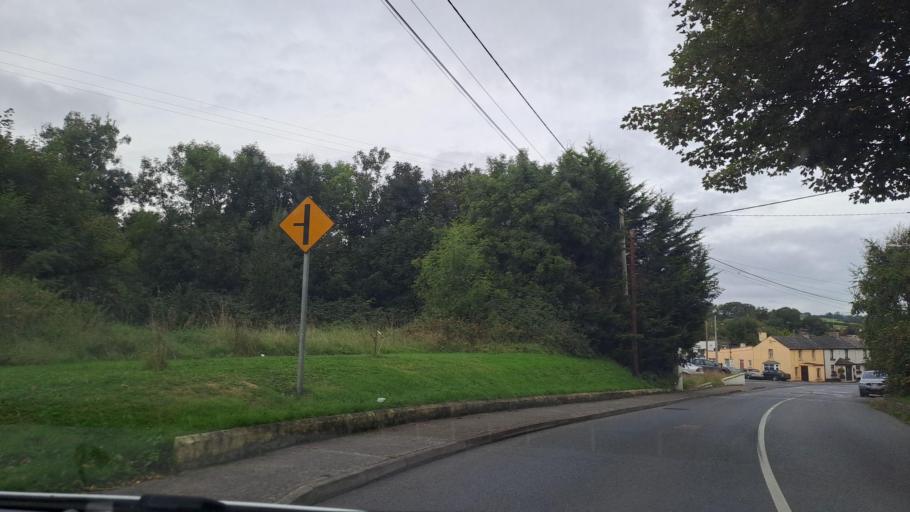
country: IE
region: Leinster
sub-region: Lu
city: Ardee
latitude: 53.8498
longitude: -6.6521
